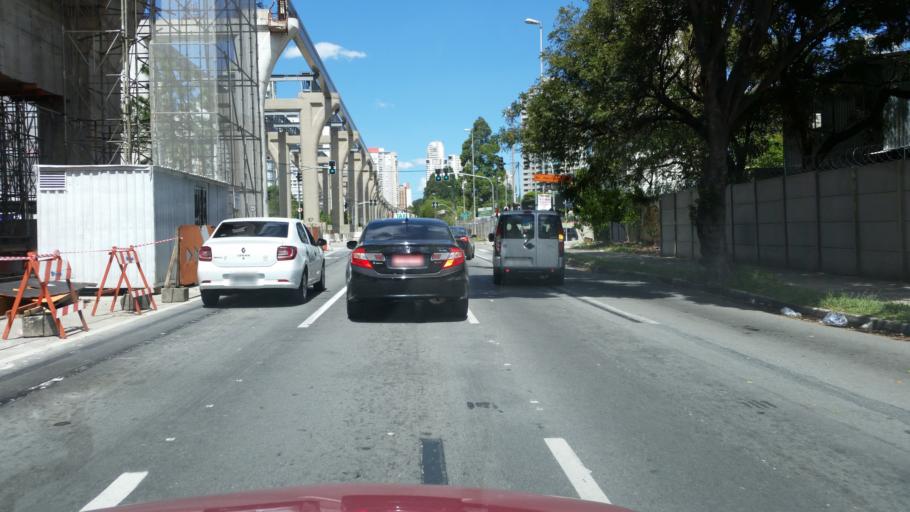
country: BR
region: Sao Paulo
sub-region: Sao Paulo
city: Sao Paulo
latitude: -23.6187
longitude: -46.6835
